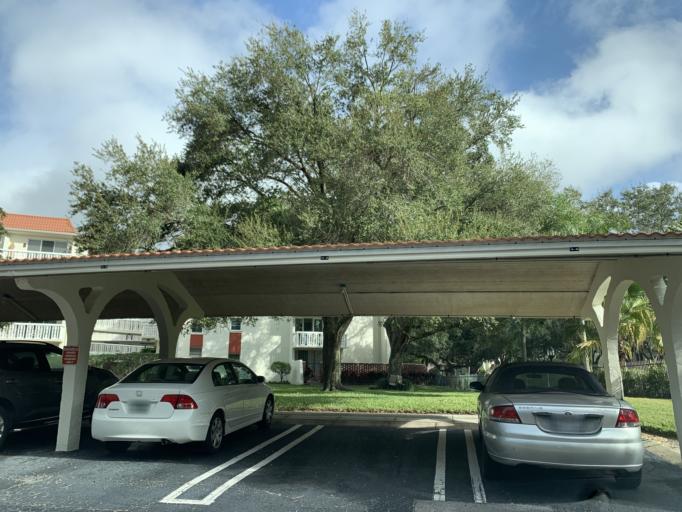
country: US
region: Florida
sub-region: Pinellas County
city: South Highpoint
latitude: 27.9533
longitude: -82.7250
